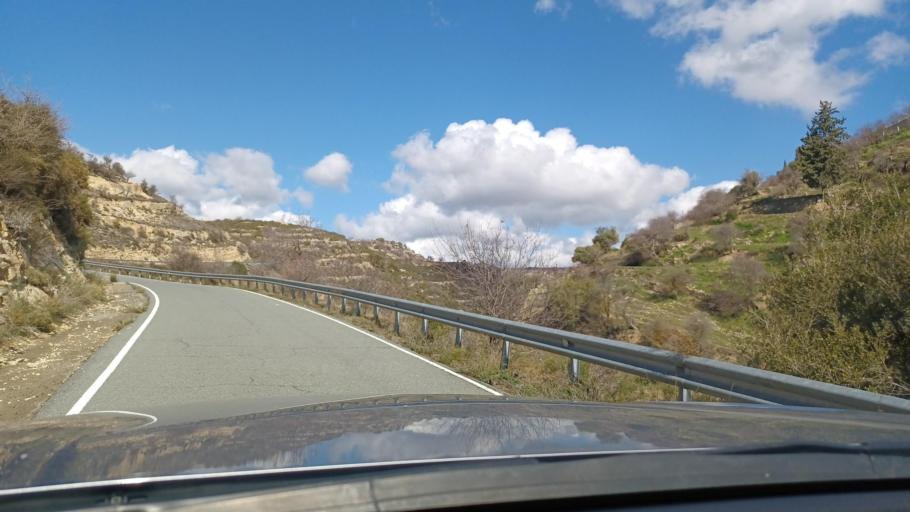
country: CY
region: Limassol
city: Pachna
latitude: 34.8185
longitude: 32.7787
